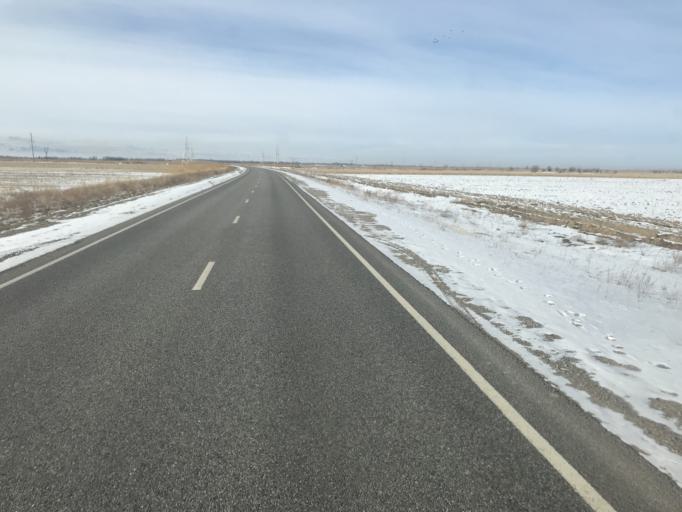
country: KZ
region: Zhambyl
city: Taraz
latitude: 43.0066
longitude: 71.2695
